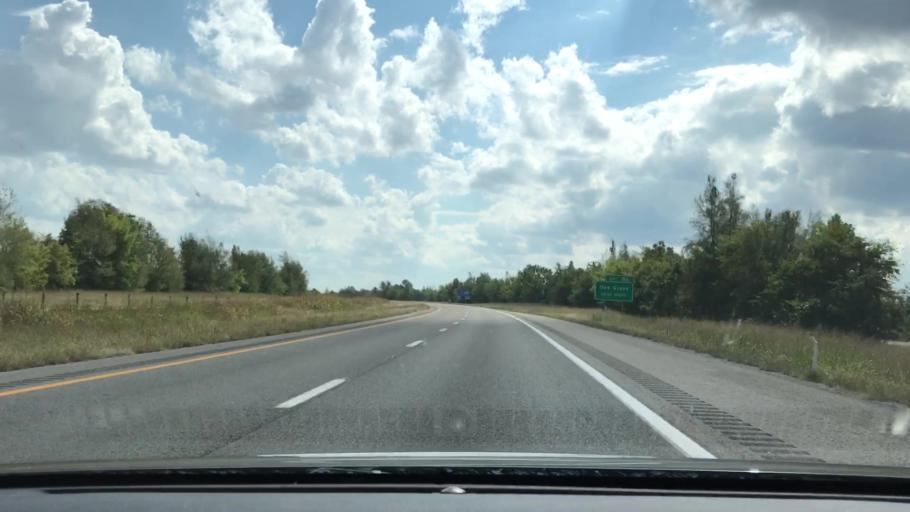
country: US
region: Kentucky
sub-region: Christian County
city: Oak Grove
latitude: 36.7182
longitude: -87.4840
